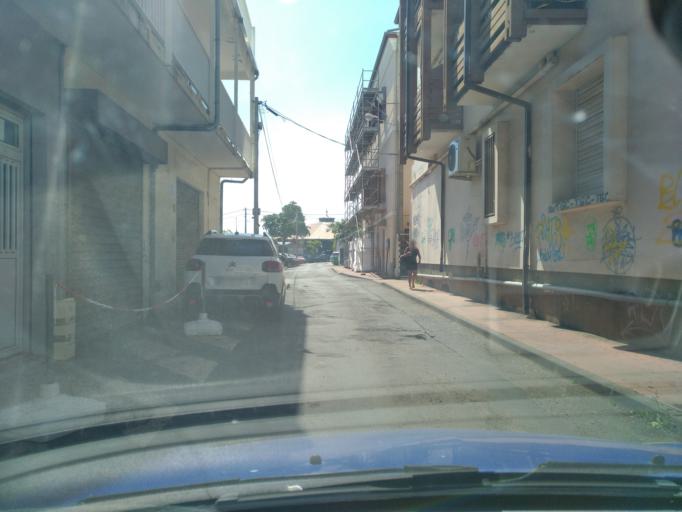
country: RE
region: Reunion
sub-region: Reunion
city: Saint-Pierre
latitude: -21.3412
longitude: 55.4750
